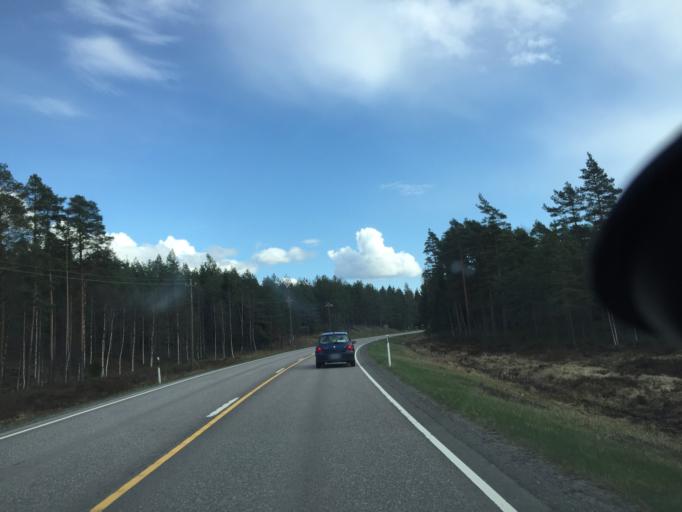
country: FI
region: Uusimaa
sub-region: Raaseporin
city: Ekenaes
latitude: 60.0160
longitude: 23.3886
